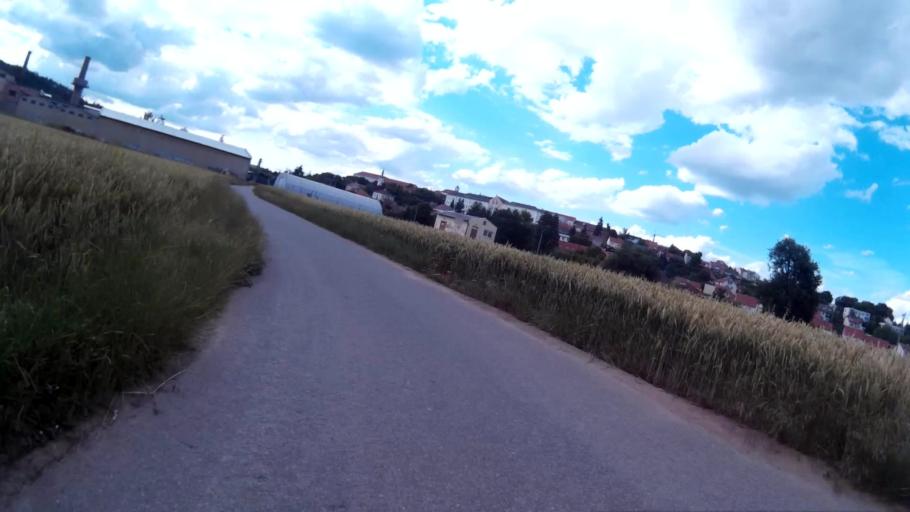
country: CZ
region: South Moravian
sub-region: Okres Brno-Venkov
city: Rosice
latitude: 49.1773
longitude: 16.3911
